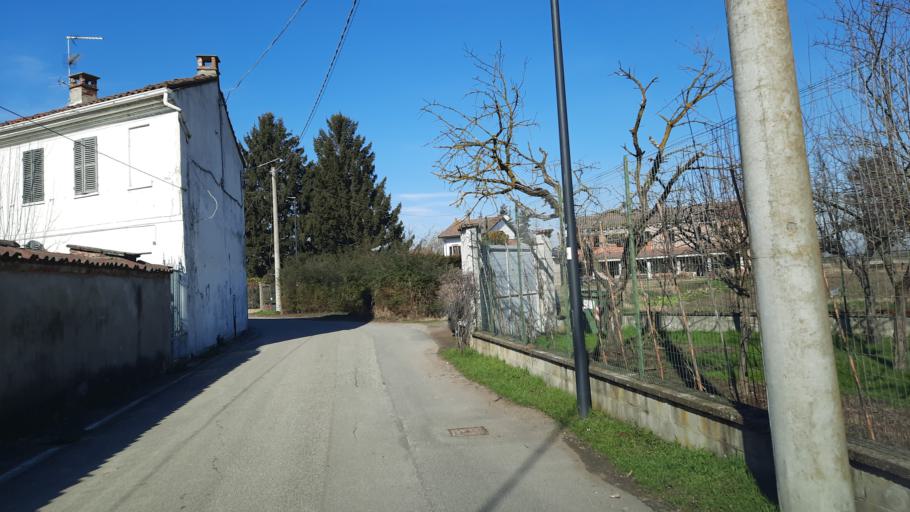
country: IT
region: Piedmont
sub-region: Provincia di Vercelli
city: Pertengo
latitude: 45.2359
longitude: 8.4190
